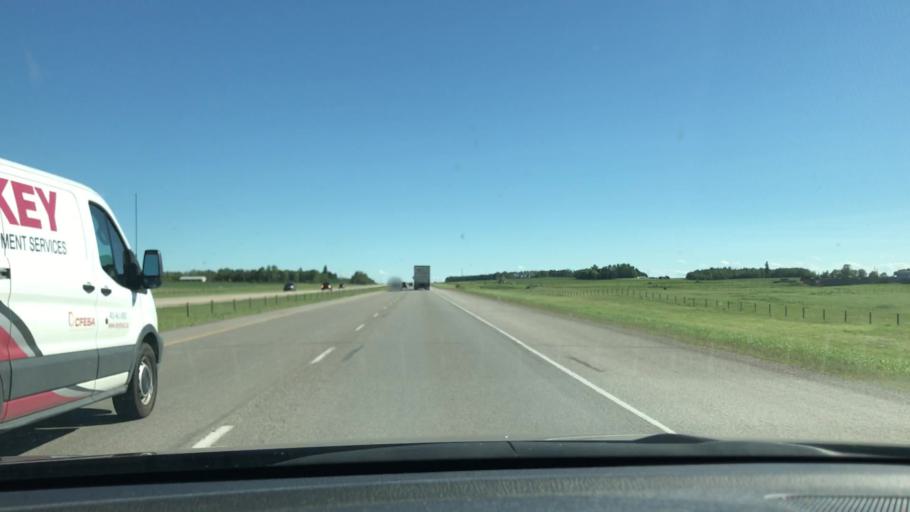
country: CA
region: Alberta
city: Olds
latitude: 51.8950
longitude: -114.0252
